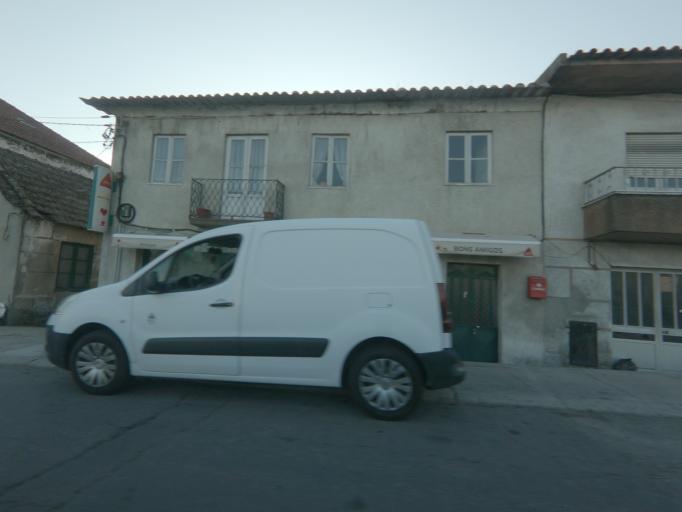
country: PT
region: Vila Real
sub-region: Vila Real
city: Vila Real
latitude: 41.3131
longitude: -7.7339
